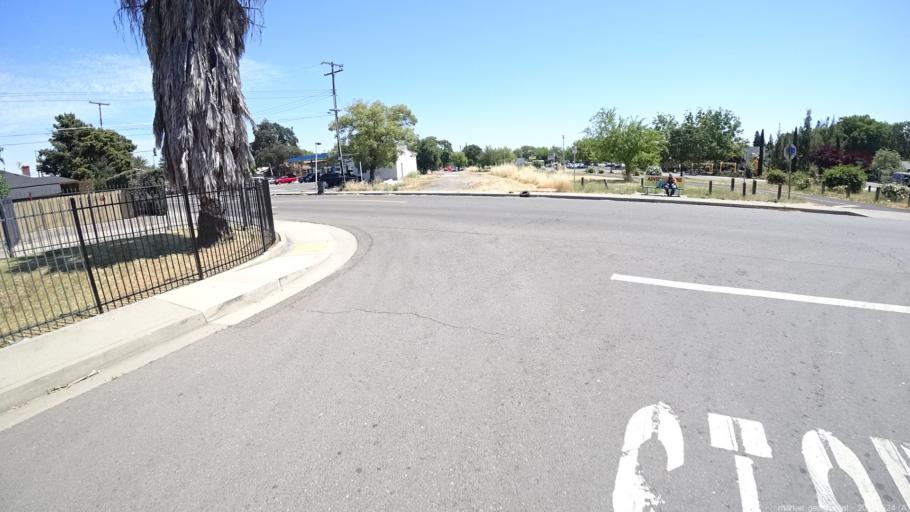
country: US
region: California
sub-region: Sacramento County
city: Sacramento
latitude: 38.6104
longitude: -121.4595
